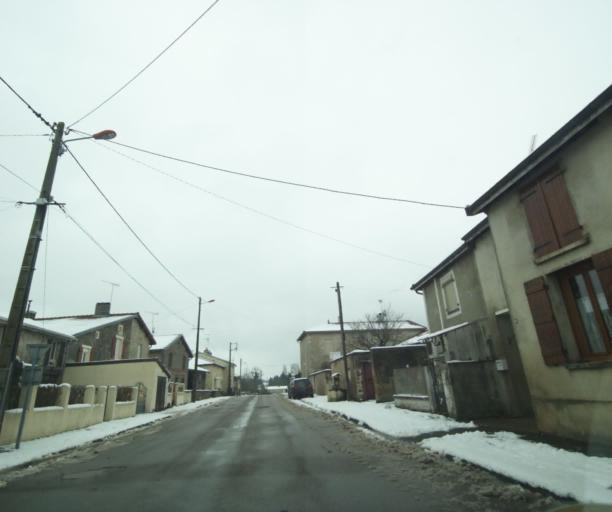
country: FR
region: Champagne-Ardenne
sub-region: Departement de la Haute-Marne
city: Laneuville-a-Remy
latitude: 48.4105
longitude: 4.8428
